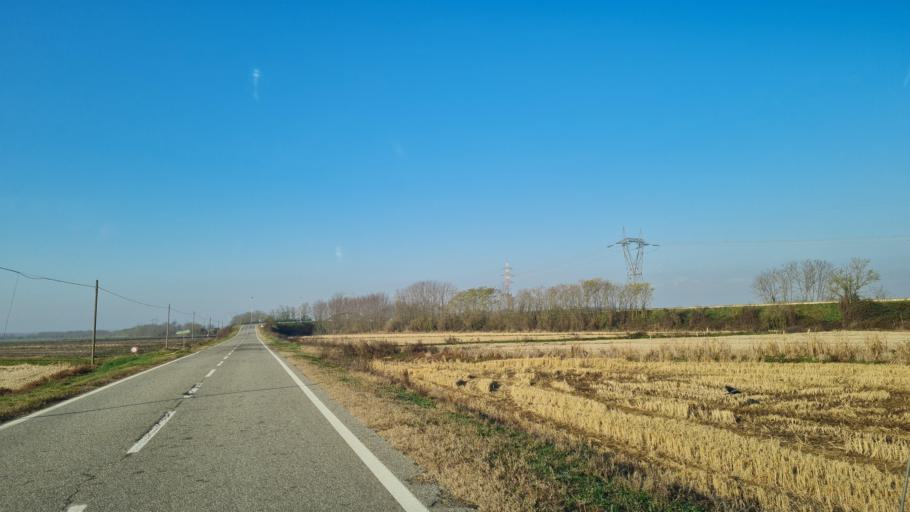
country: IT
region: Piedmont
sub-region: Provincia di Vercelli
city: Formigliana
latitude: 45.4468
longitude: 8.3112
